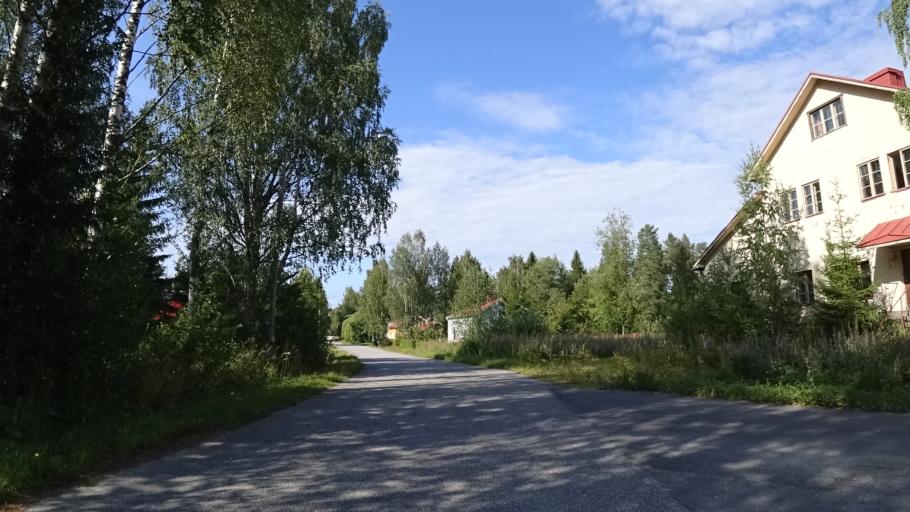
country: FI
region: North Karelia
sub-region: Joensuu
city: Eno
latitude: 62.7988
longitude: 30.1506
